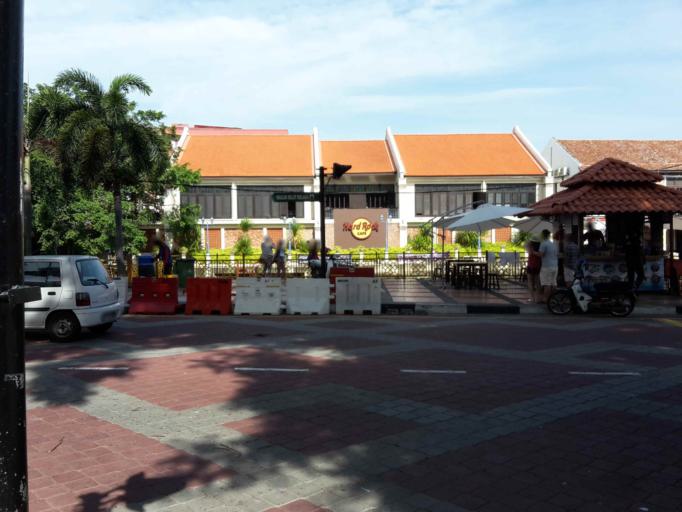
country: MY
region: Melaka
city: Malacca
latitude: 2.1945
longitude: 102.2491
